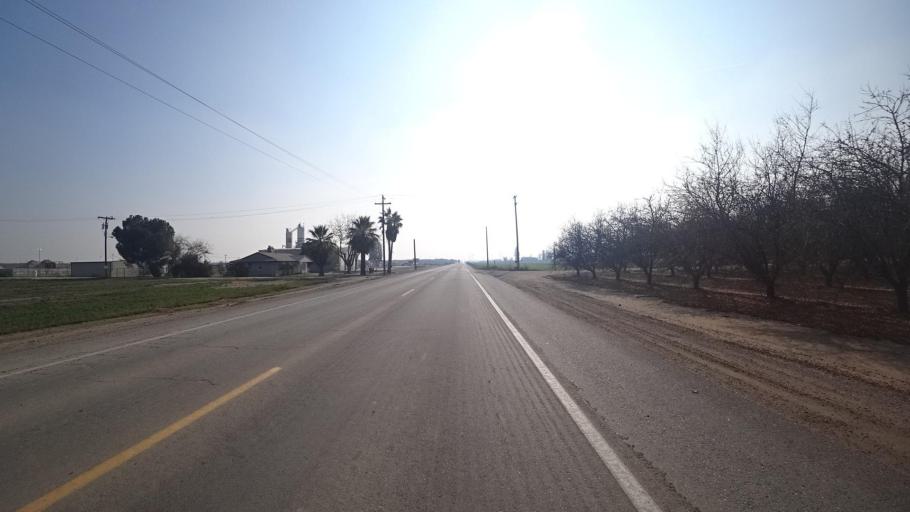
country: US
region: California
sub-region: Kern County
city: Greenfield
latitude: 35.2531
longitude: -119.1098
